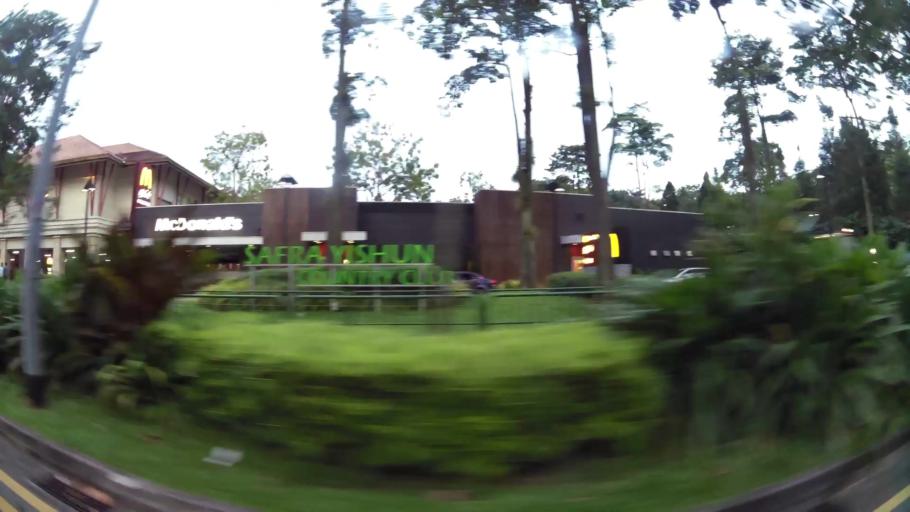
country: MY
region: Johor
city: Kampung Pasir Gudang Baru
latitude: 1.4231
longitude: 103.8408
